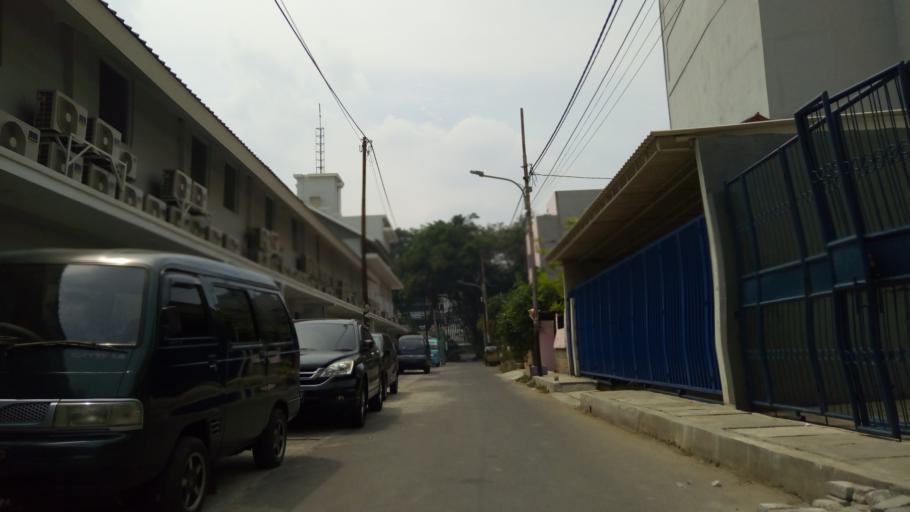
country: ID
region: Jakarta Raya
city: Jakarta
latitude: -6.1626
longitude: 106.8368
